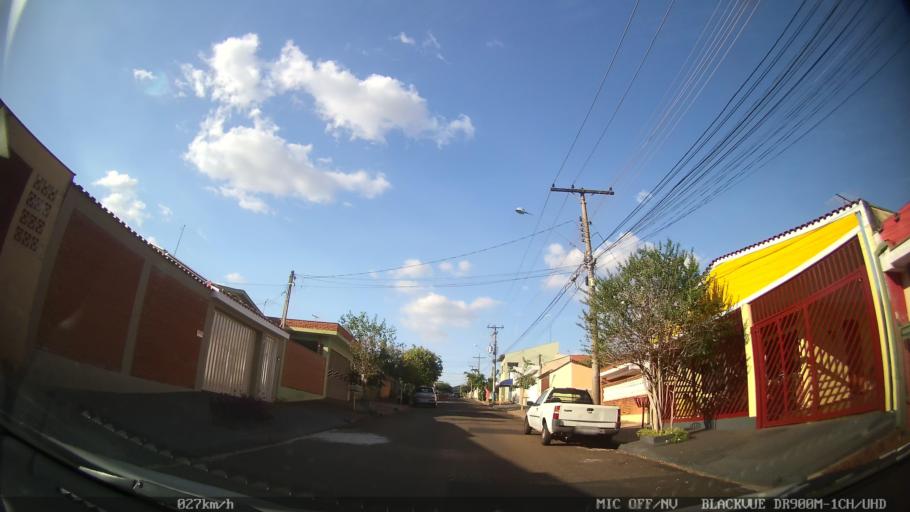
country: BR
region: Sao Paulo
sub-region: Ribeirao Preto
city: Ribeirao Preto
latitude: -21.1901
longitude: -47.7890
